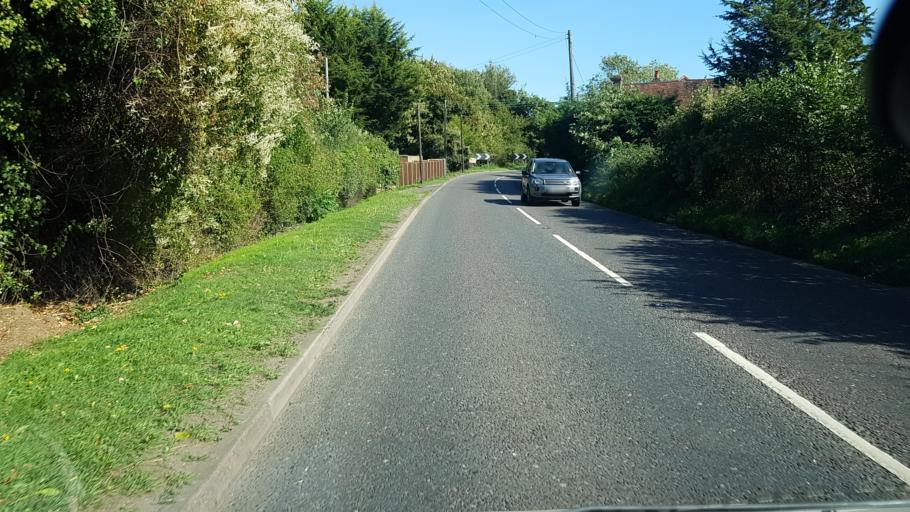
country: GB
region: England
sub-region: Kent
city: Kings Hill
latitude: 51.2534
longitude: 0.3755
